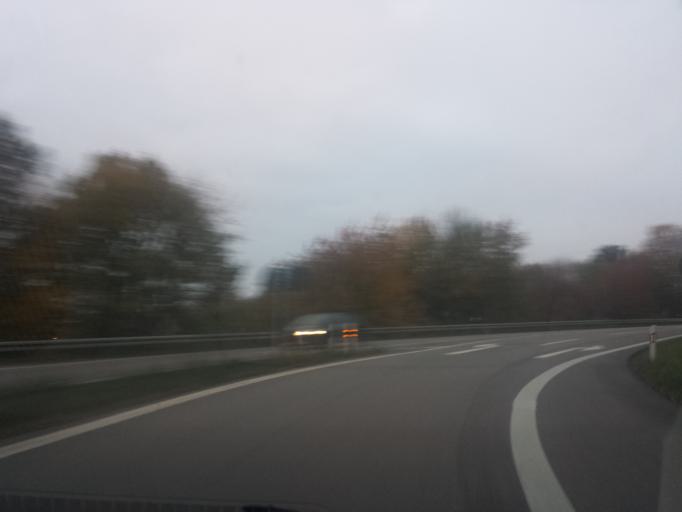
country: DE
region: Bavaria
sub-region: Upper Bavaria
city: Hepberg
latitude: 48.8149
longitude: 11.4652
